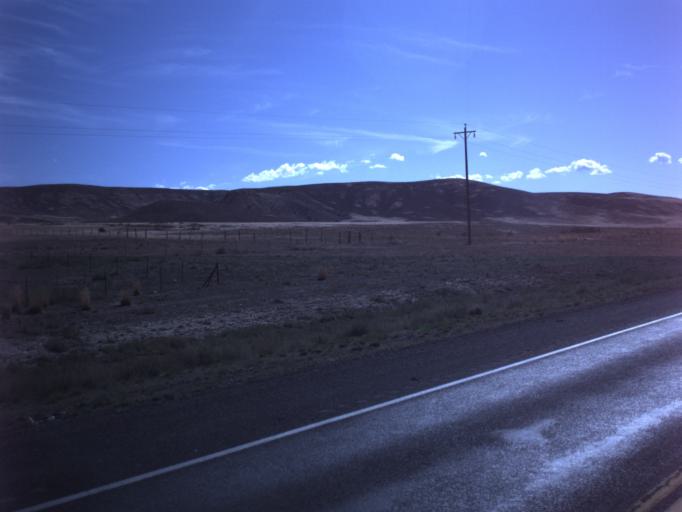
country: US
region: Utah
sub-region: Sanpete County
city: Gunnison
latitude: 39.1975
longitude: -111.8451
